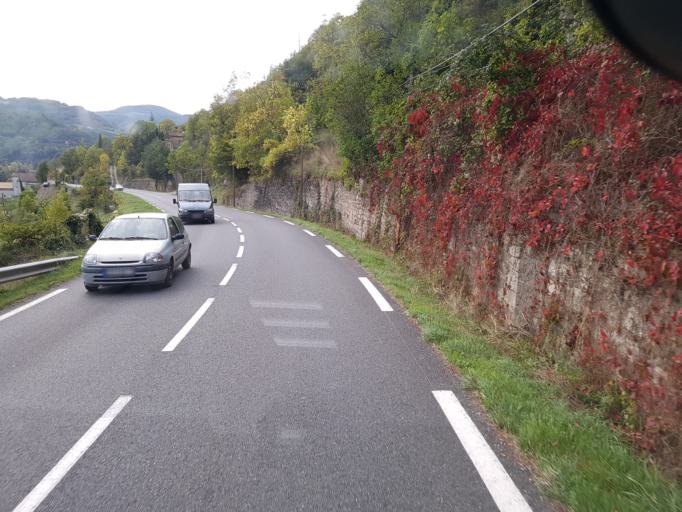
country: FR
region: Midi-Pyrenees
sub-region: Departement de l'Aveyron
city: Saint-Affrique
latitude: 43.9638
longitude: 2.8964
